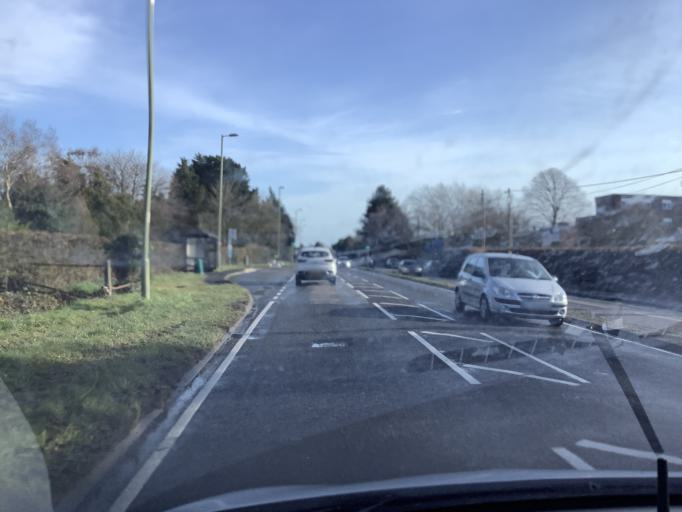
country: GB
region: England
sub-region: Hampshire
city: Hythe
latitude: 50.8380
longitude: -1.3868
